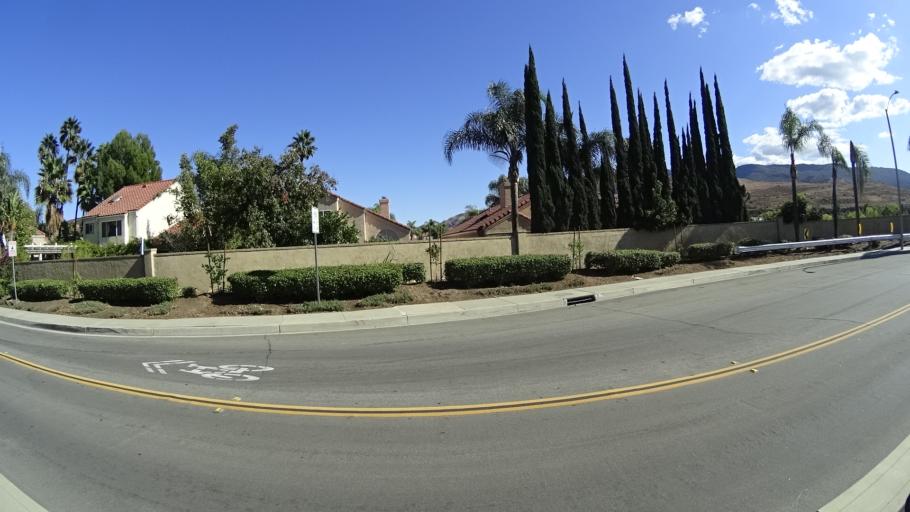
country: US
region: California
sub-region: San Bernardino County
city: Los Serranos
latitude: 33.8748
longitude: -117.7078
